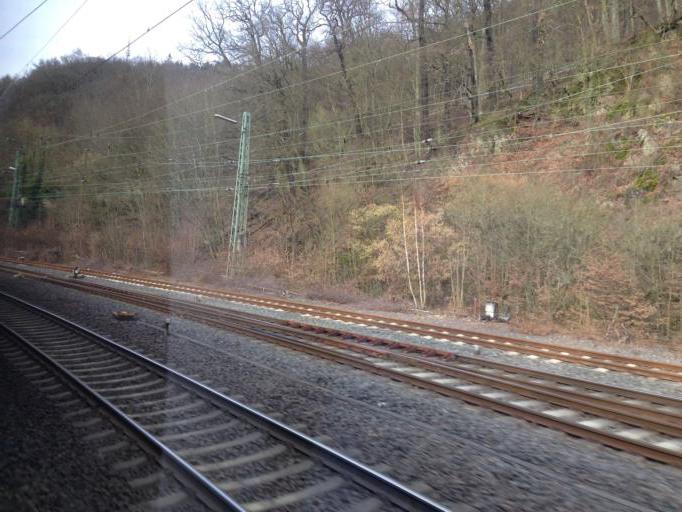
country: DE
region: Hesse
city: Dillenburg
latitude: 50.7393
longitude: 8.2924
